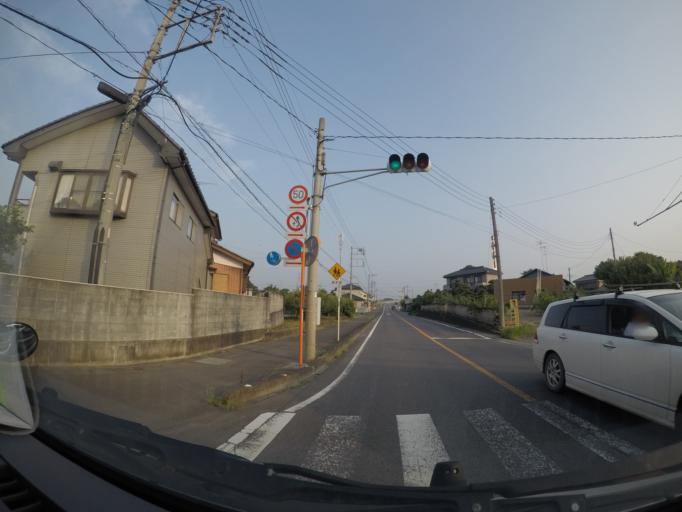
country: JP
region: Tochigi
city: Fujioka
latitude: 36.2694
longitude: 139.7153
